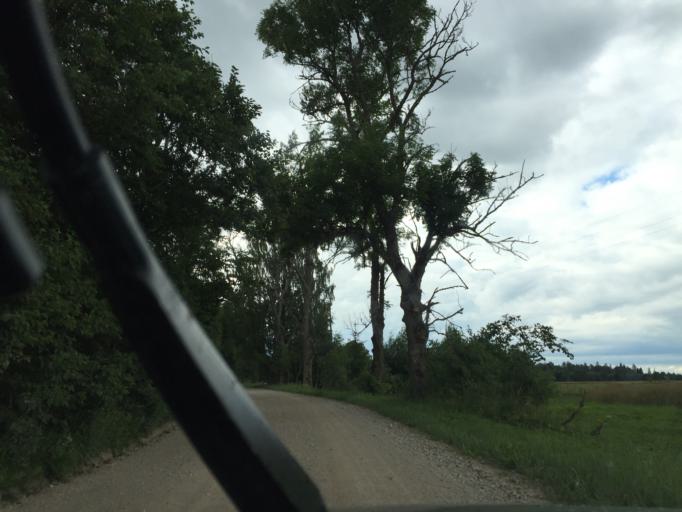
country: LV
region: Malpils
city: Malpils
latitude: 56.9384
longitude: 25.0127
